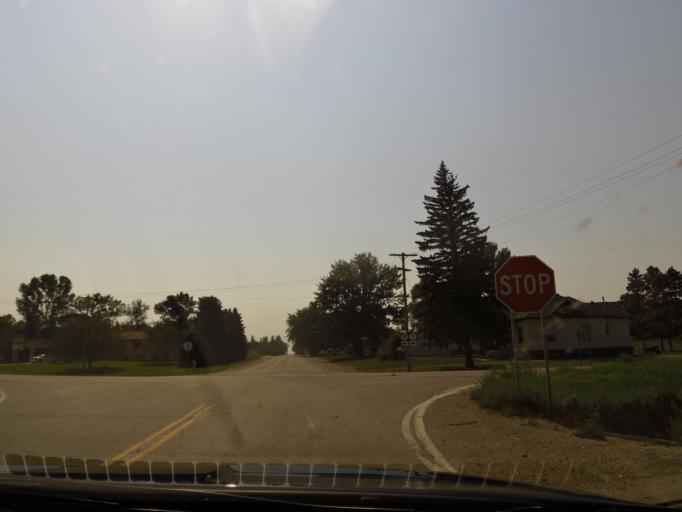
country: US
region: South Dakota
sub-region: Roberts County
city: Sisseton
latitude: 46.0785
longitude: -97.1565
